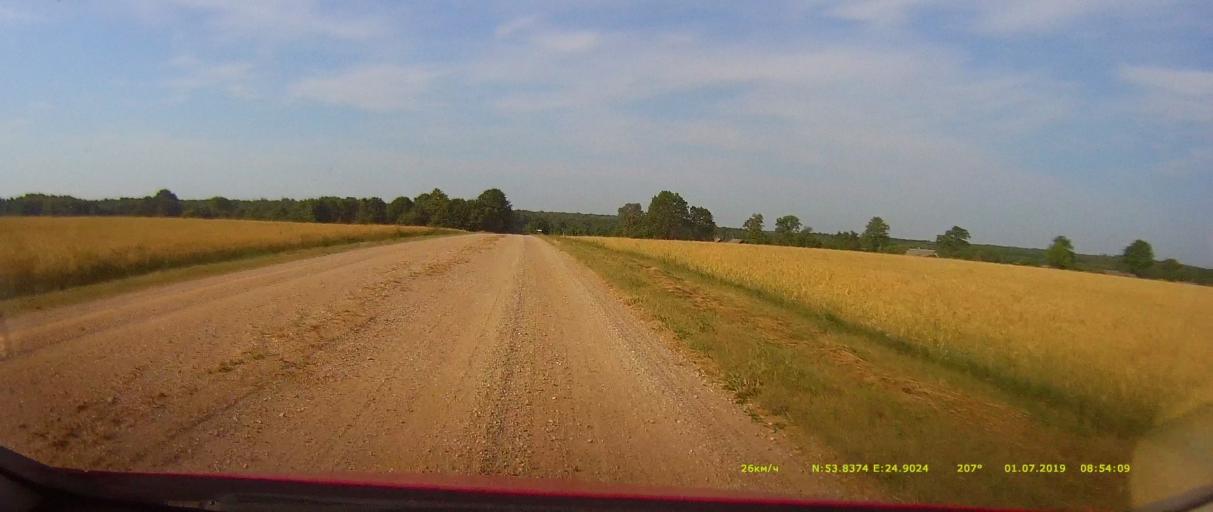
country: BY
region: Grodnenskaya
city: Shchuchin
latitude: 53.8375
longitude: 24.9025
